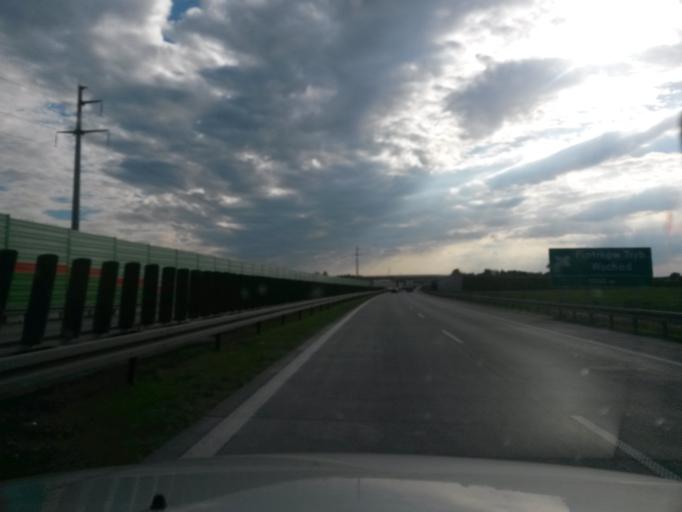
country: PL
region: Lodz Voivodeship
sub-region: Piotrkow Trybunalski
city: Piotrkow Trybunalski
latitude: 51.4453
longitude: 19.7516
